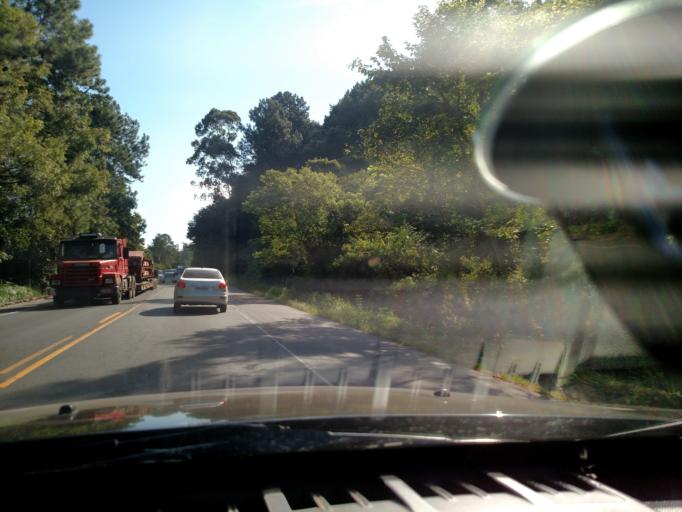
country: BR
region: Santa Catarina
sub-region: Rio Do Sul
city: Rio do Sul
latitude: -27.2606
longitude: -49.7194
